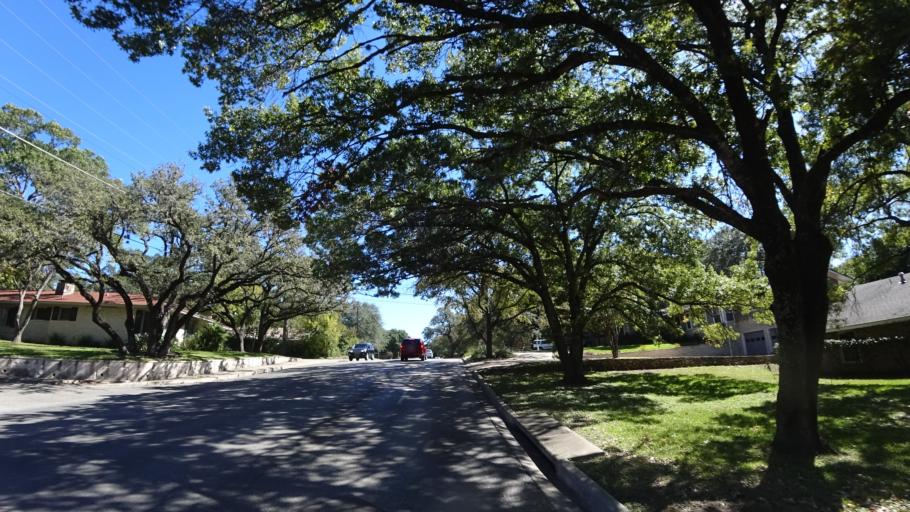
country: US
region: Texas
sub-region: Travis County
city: Austin
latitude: 30.3183
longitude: -97.7478
